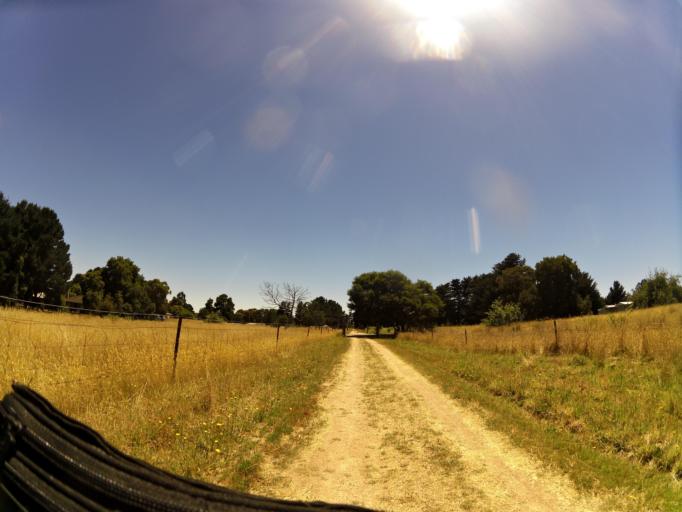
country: AU
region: Victoria
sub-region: Ballarat North
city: Delacombe
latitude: -37.6699
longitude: 143.6565
